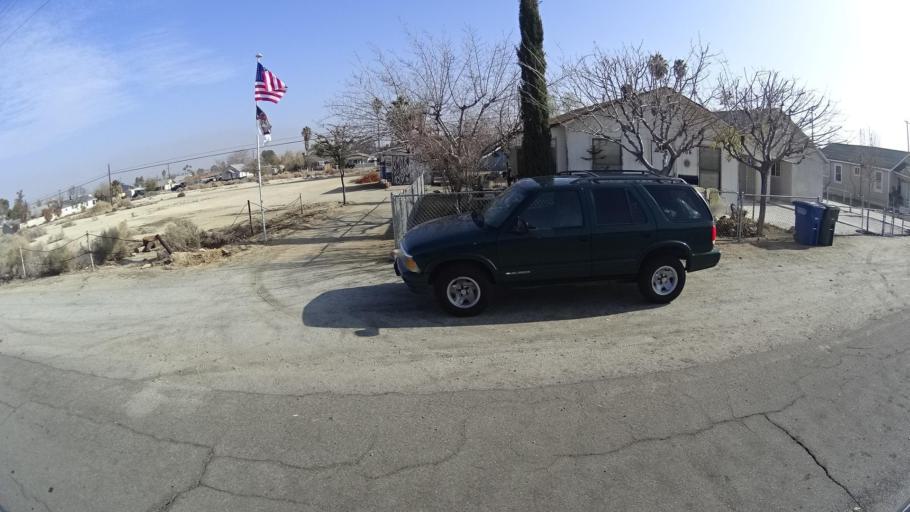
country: US
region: California
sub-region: Kern County
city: Ford City
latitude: 35.1612
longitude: -119.4653
